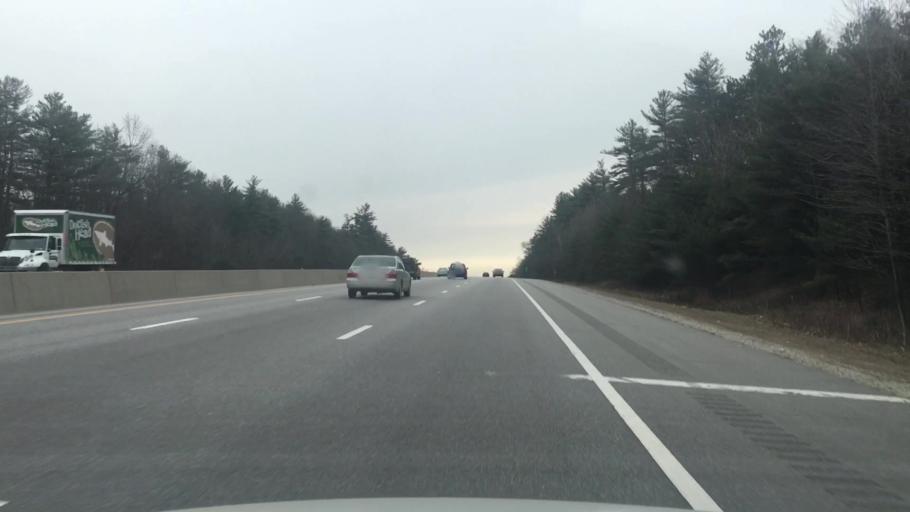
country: US
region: New Hampshire
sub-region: Merrimack County
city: Bow Bog
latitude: 43.1505
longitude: -71.5044
